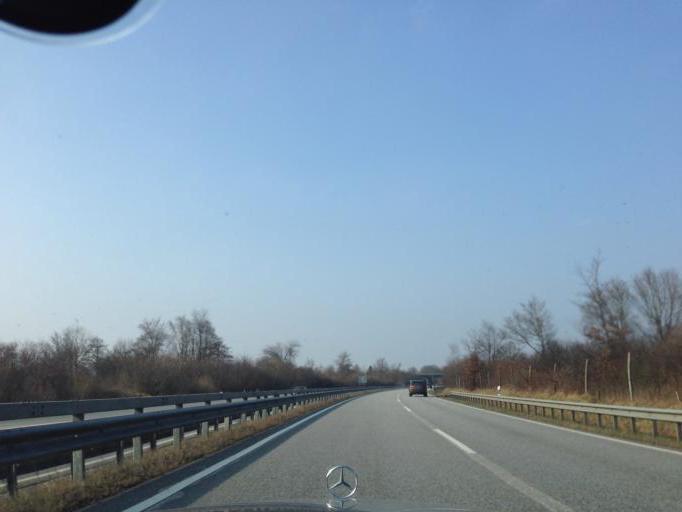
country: DE
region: Schleswig-Holstein
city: Negernbotel
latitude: 53.9708
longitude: 10.2425
